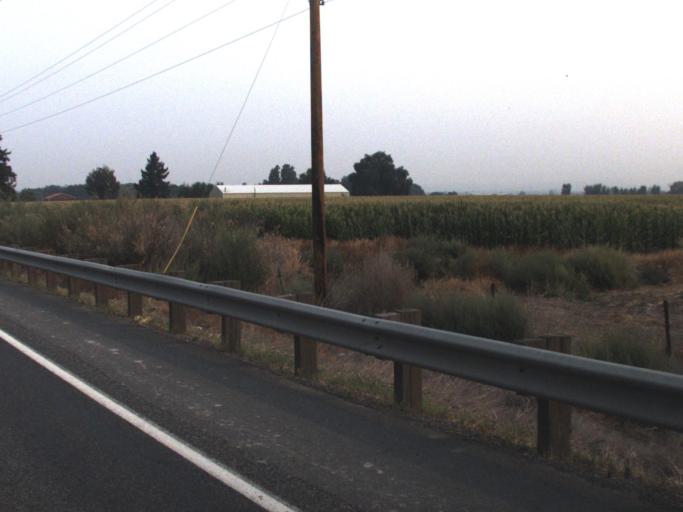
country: US
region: Washington
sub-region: Yakima County
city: Toppenish
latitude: 46.3500
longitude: -120.3205
